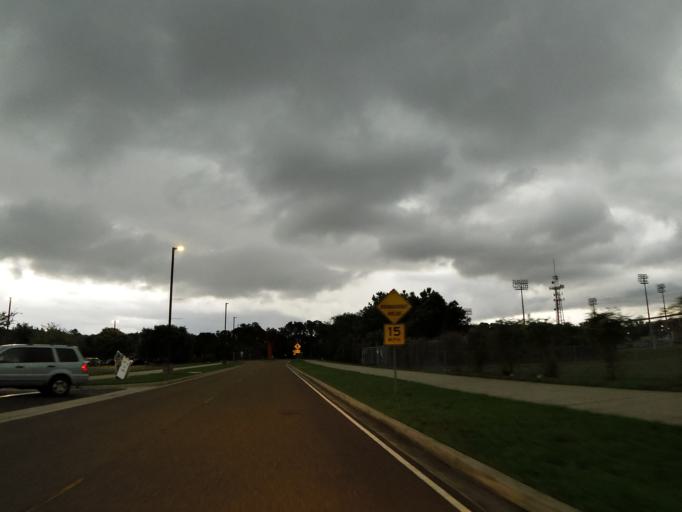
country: US
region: Florida
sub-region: Duval County
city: Jacksonville Beach
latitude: 30.2762
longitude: -81.5110
